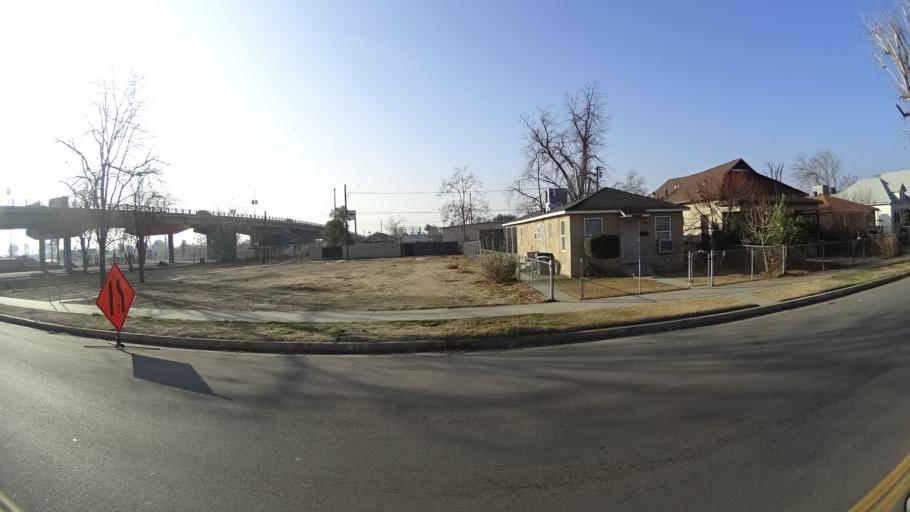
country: US
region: California
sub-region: Kern County
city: Bakersfield
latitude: 35.3783
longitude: -118.9897
